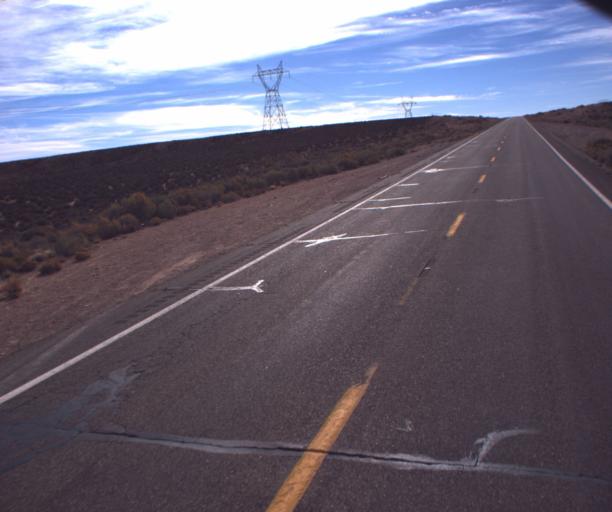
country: US
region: Arizona
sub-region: Coconino County
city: LeChee
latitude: 36.8029
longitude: -111.3043
